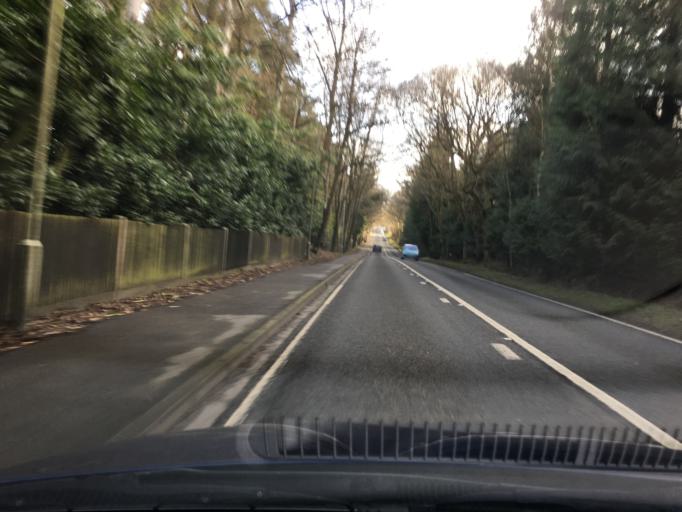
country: GB
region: England
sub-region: Bracknell Forest
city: Crowthorne
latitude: 51.3783
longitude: -0.7807
